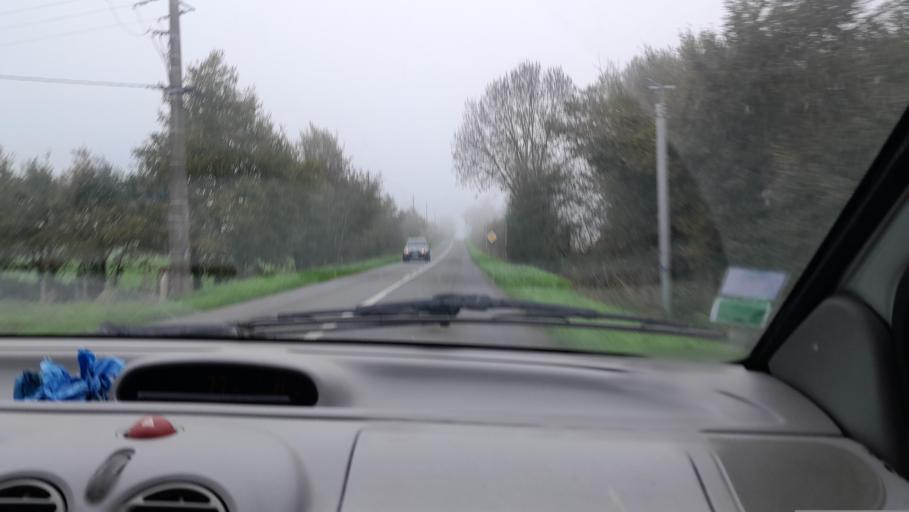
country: FR
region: Pays de la Loire
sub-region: Departement de la Mayenne
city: Ahuille
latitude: 48.0365
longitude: -0.8966
